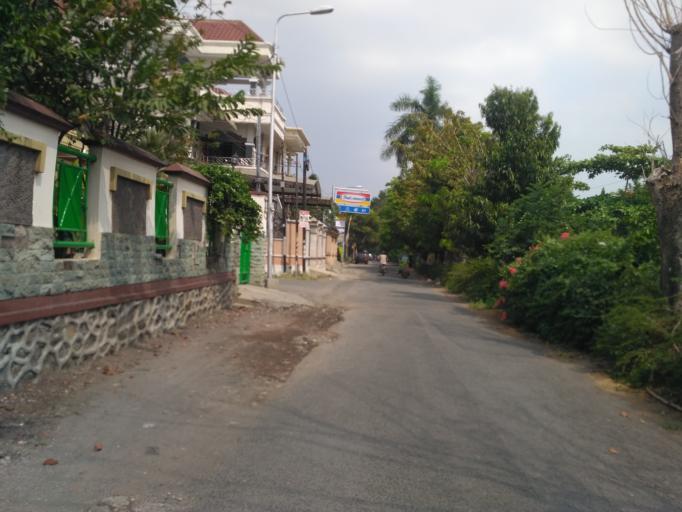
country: ID
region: Central Java
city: Semarang
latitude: -6.9913
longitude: 110.4368
